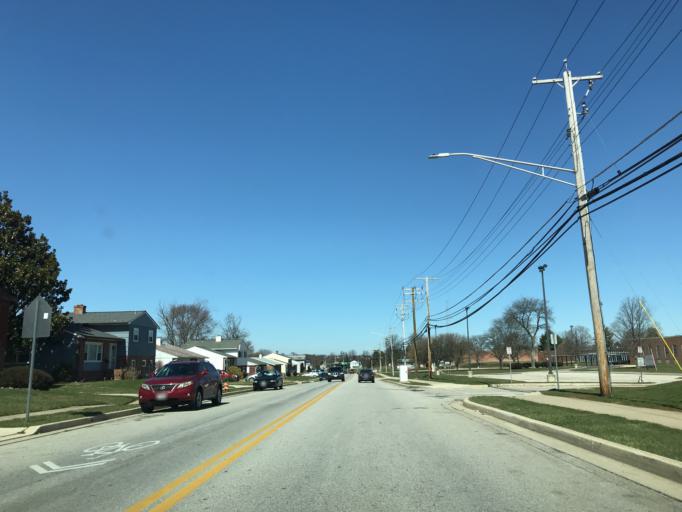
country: US
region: Maryland
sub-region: Baltimore County
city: Woodlawn
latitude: 39.2980
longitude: -76.7357
